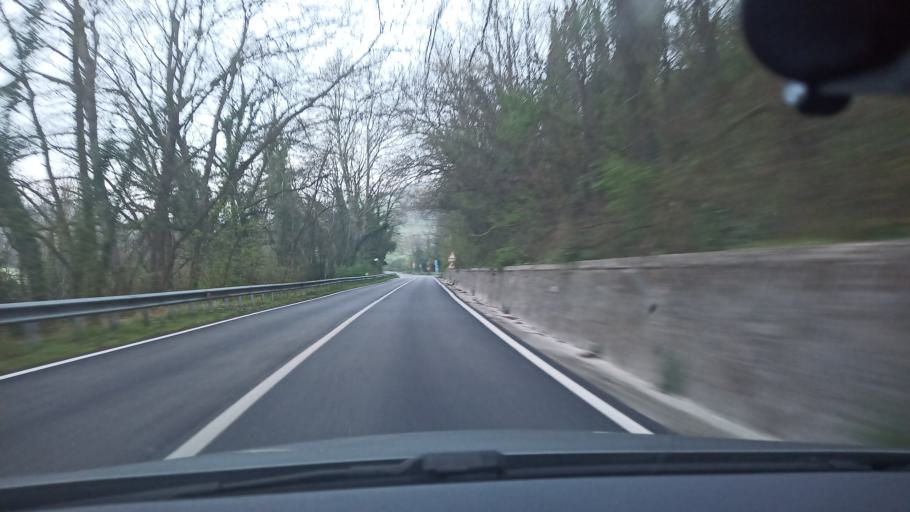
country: IT
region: Latium
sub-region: Provincia di Rieti
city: Cantalupo in Sabina
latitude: 42.2858
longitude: 12.6536
